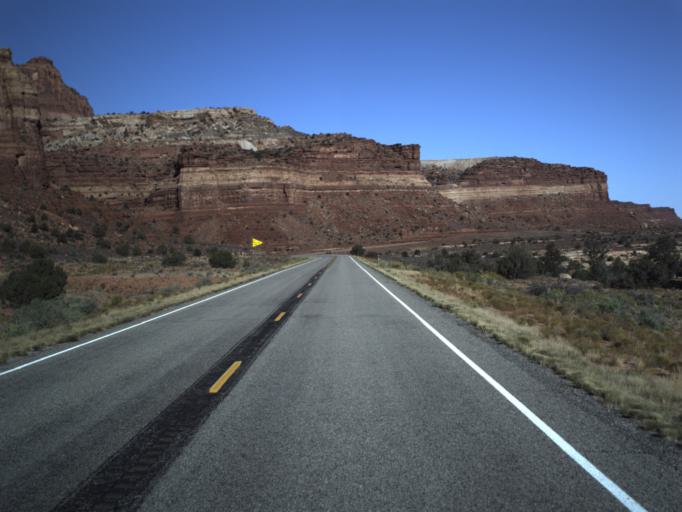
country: US
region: Utah
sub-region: San Juan County
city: Blanding
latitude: 37.7389
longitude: -110.2745
